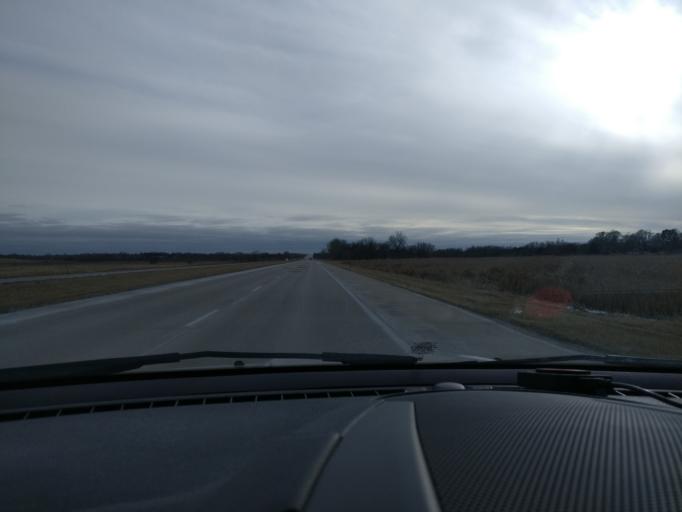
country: US
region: Nebraska
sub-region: Lancaster County
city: Waverly
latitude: 41.0348
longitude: -96.6403
